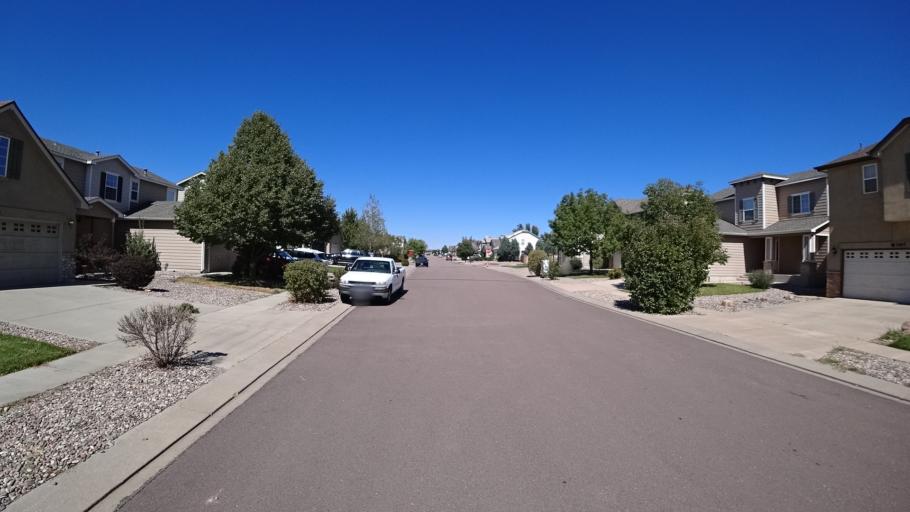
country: US
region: Colorado
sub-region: El Paso County
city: Security-Widefield
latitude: 38.7824
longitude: -104.7347
